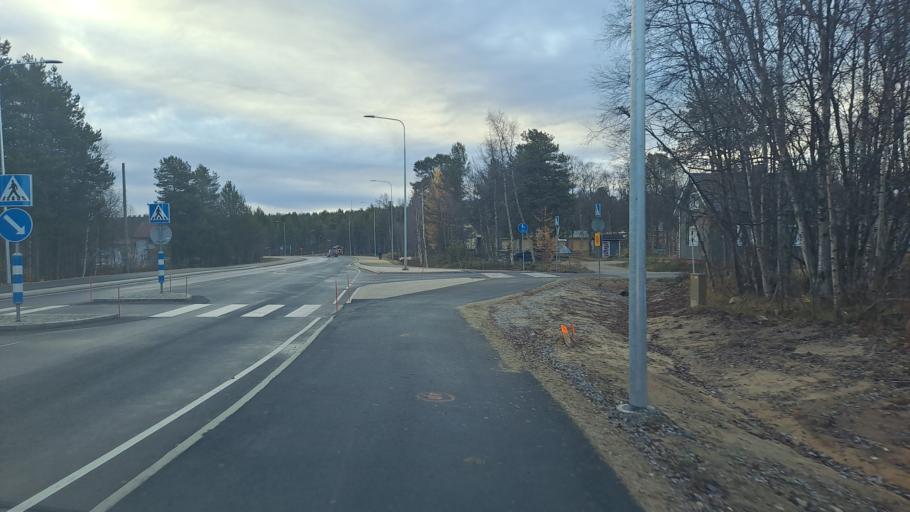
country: FI
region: Lapland
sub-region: Pohjois-Lappi
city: Inari
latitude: 68.9036
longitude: 27.0328
